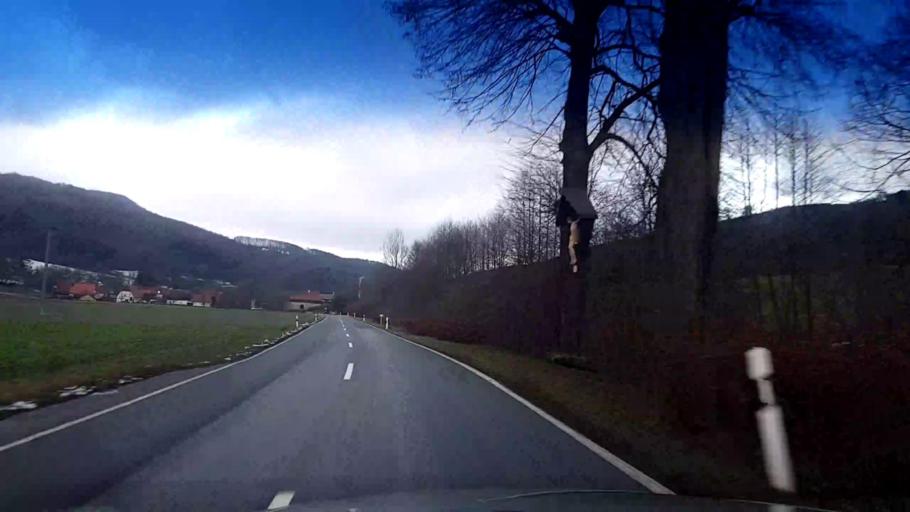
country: DE
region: Bavaria
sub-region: Upper Franconia
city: Buttenheim
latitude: 49.8274
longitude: 11.0794
